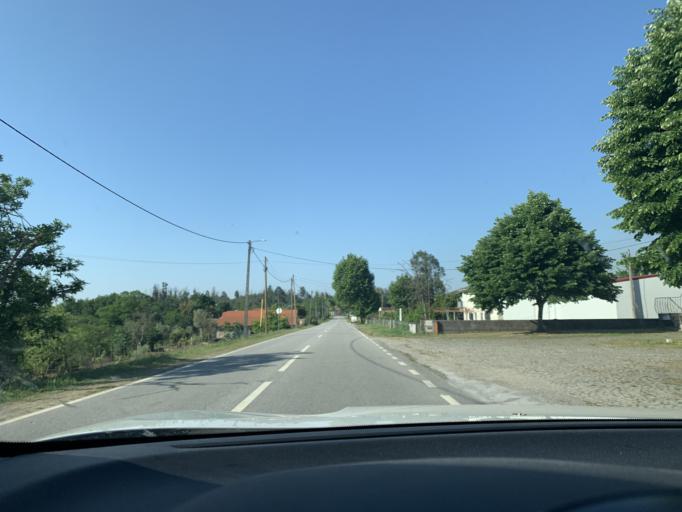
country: PT
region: Viseu
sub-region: Concelho de Tondela
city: Tondela
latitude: 40.4800
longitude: -8.0912
